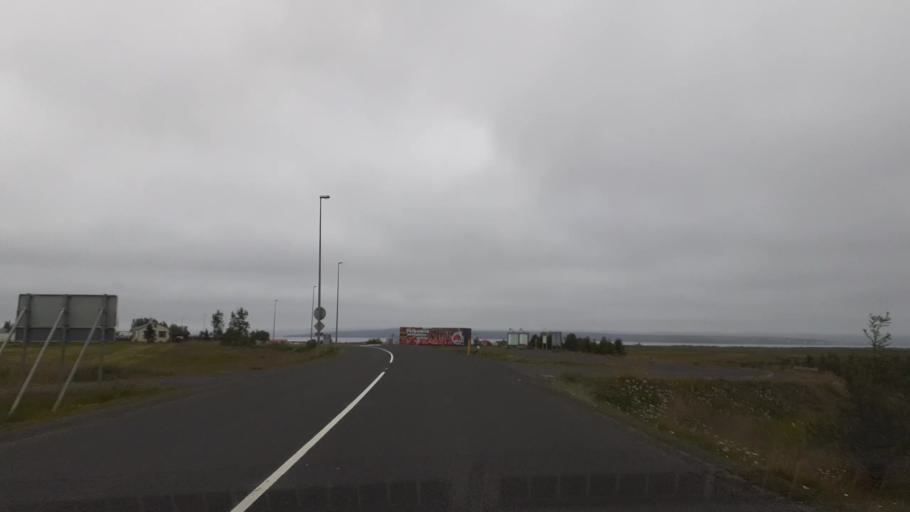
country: IS
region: Northeast
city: Dalvik
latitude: 65.9630
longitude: -18.5359
